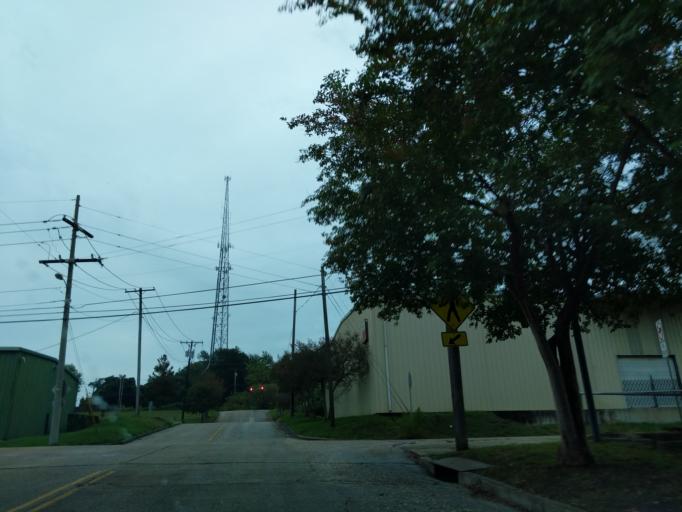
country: US
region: Mississippi
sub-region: Warren County
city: Vicksburg
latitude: 32.3454
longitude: -90.8847
